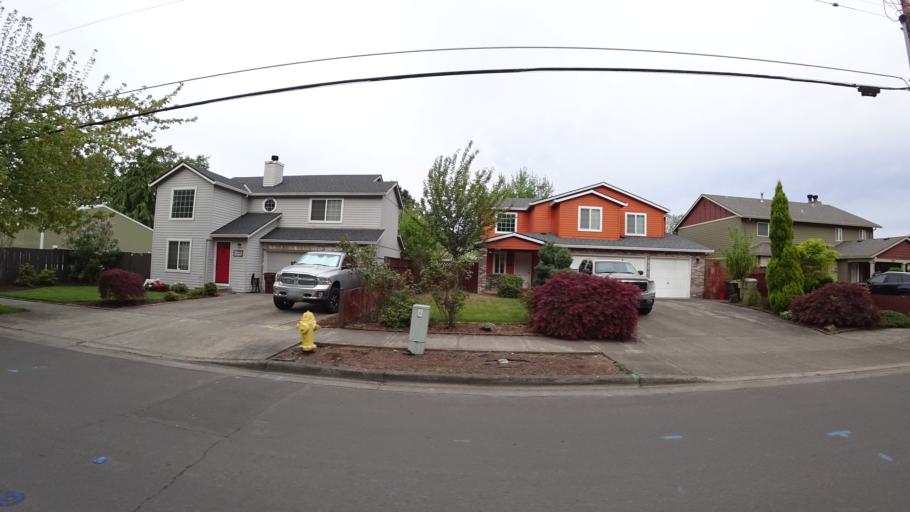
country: US
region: Oregon
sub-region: Washington County
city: Aloha
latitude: 45.5132
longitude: -122.9145
